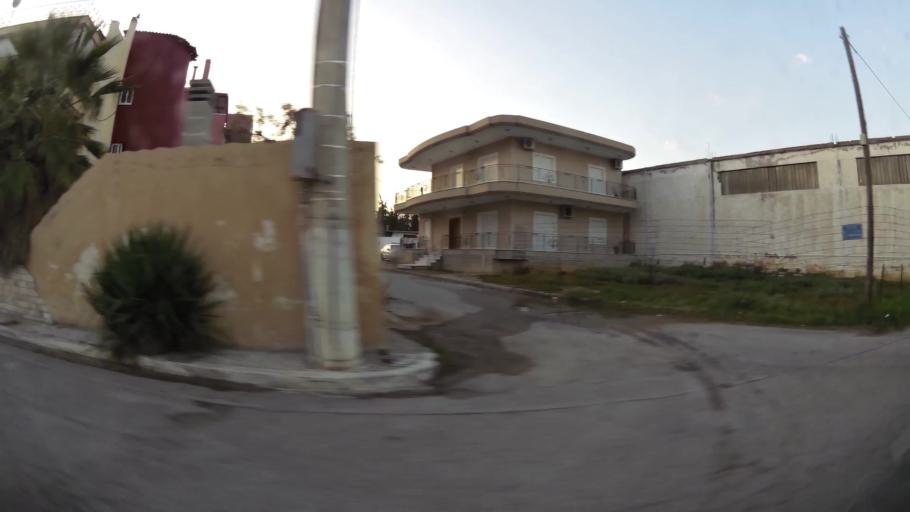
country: GR
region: Attica
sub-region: Nomarchia Anatolikis Attikis
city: Acharnes
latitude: 38.0932
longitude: 23.7509
